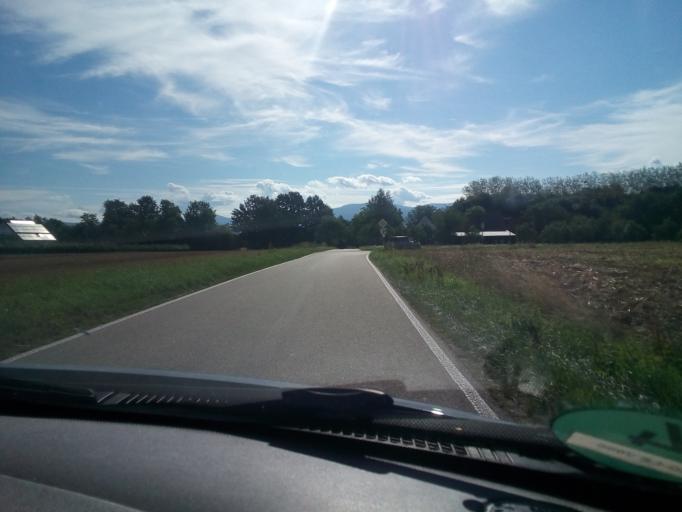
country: DE
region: Baden-Wuerttemberg
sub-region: Karlsruhe Region
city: Zell
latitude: 48.6645
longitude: 8.0361
